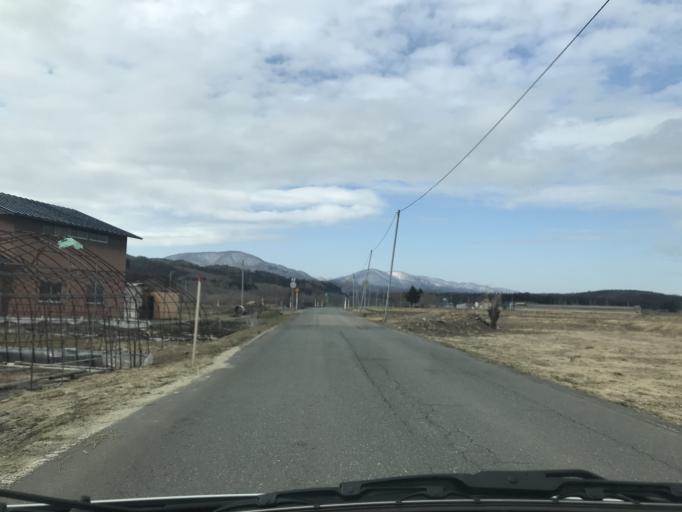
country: JP
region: Iwate
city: Hanamaki
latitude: 39.3398
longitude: 140.9829
